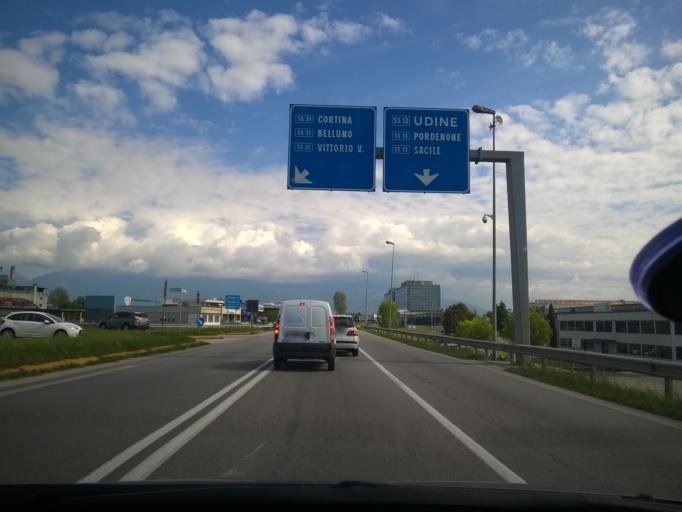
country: IT
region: Veneto
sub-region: Provincia di Treviso
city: San Vendemiano-Fossamerlo
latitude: 45.8991
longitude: 12.3321
